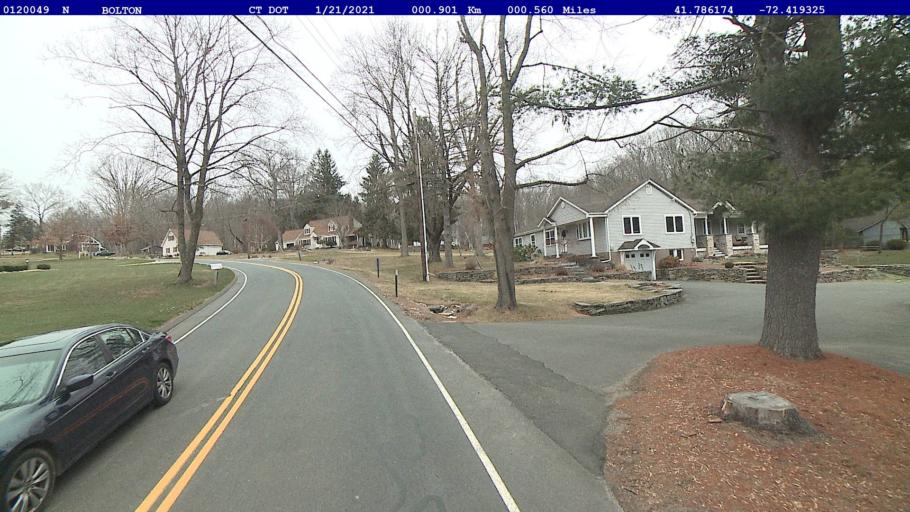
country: US
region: Connecticut
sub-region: Tolland County
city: Rockville
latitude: 41.7862
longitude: -72.4194
